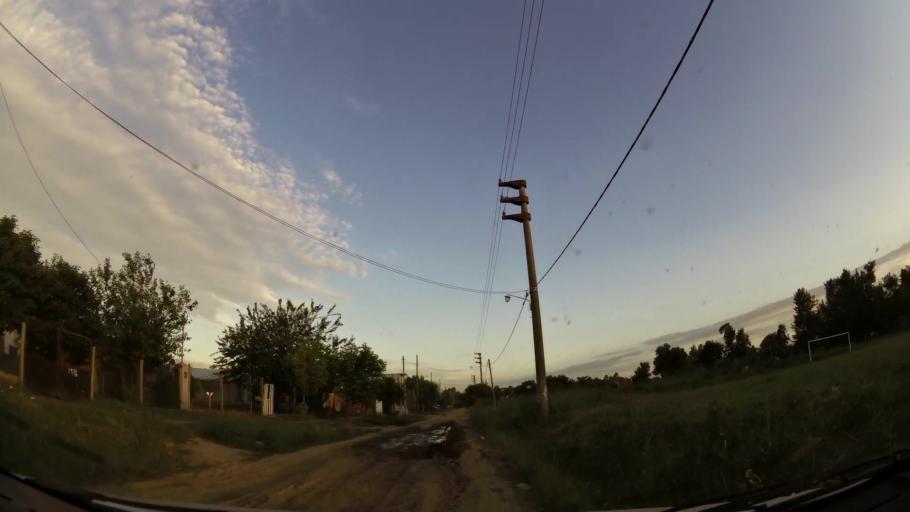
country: AR
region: Buenos Aires
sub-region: Partido de Merlo
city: Merlo
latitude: -34.6709
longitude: -58.7836
